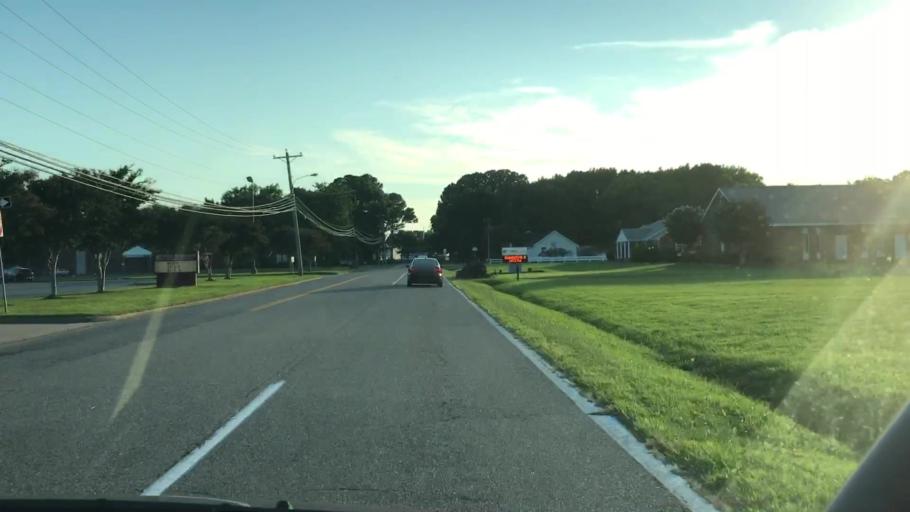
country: US
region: Virginia
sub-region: City of Hampton
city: Hampton
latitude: 37.0562
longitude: -76.3735
